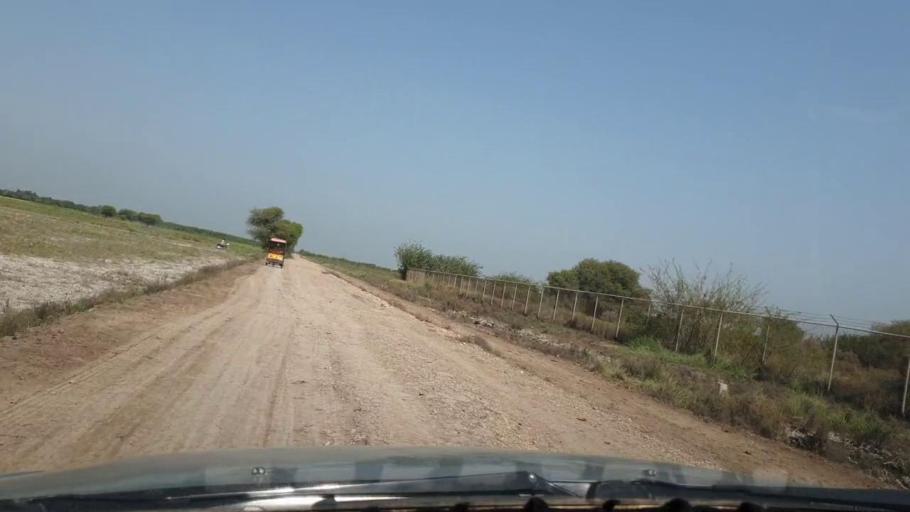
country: PK
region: Sindh
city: Tando Muhammad Khan
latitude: 25.1583
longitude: 68.6337
